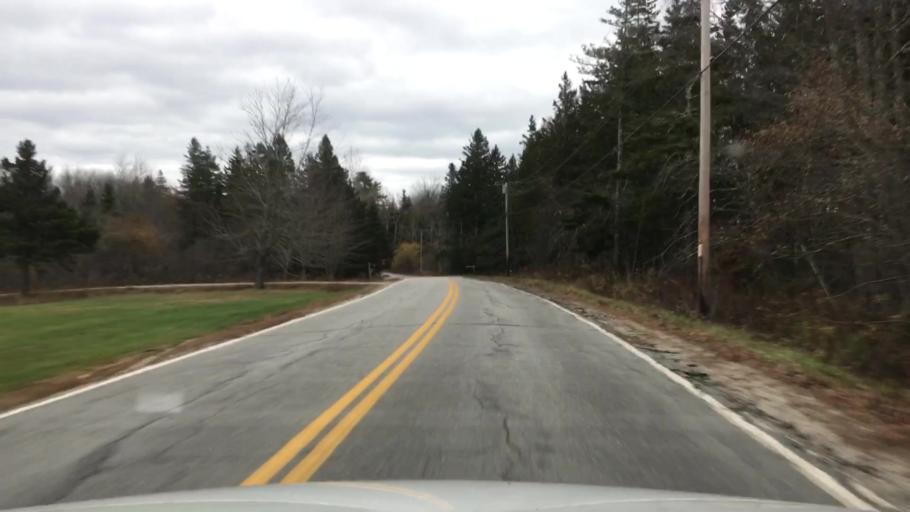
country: US
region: Maine
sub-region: Hancock County
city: Sedgwick
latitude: 44.2768
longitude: -68.5570
